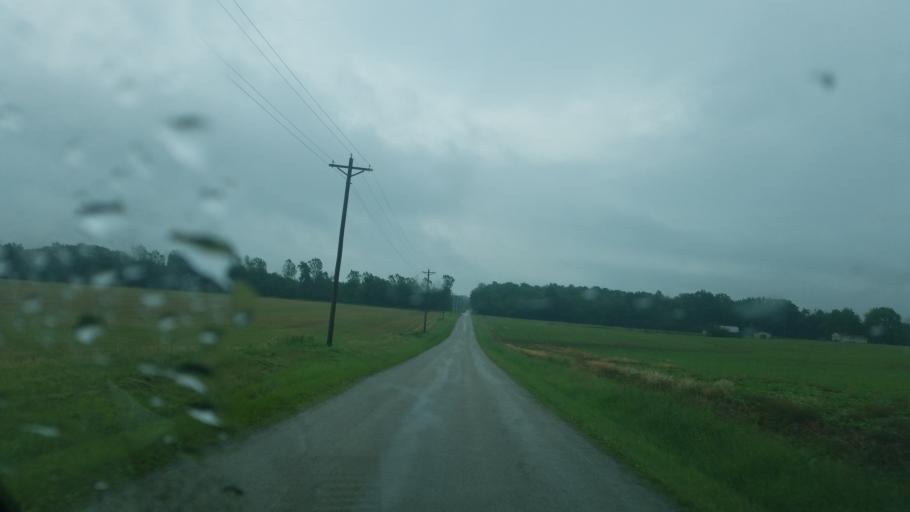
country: US
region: Ohio
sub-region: Huron County
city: Plymouth
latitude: 40.9451
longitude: -82.7289
